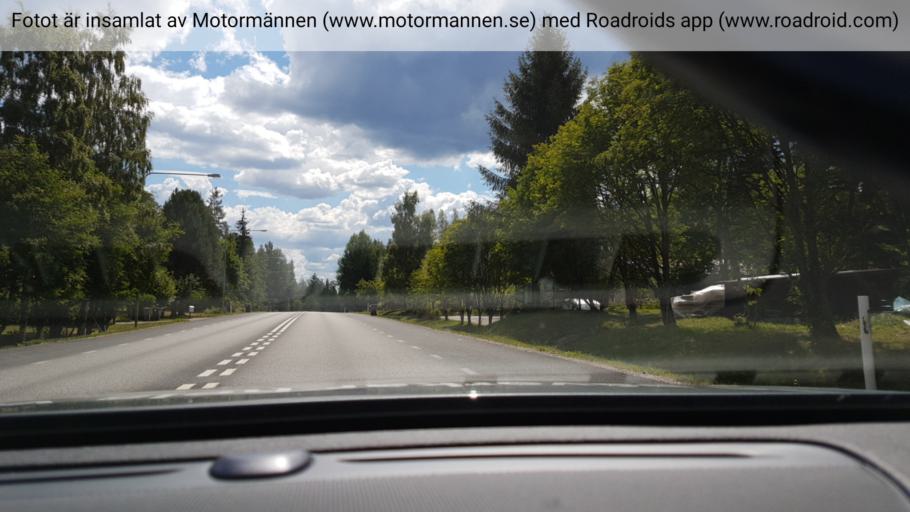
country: SE
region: Dalarna
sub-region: Faluns Kommun
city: Bjursas
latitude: 60.7300
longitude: 15.4426
